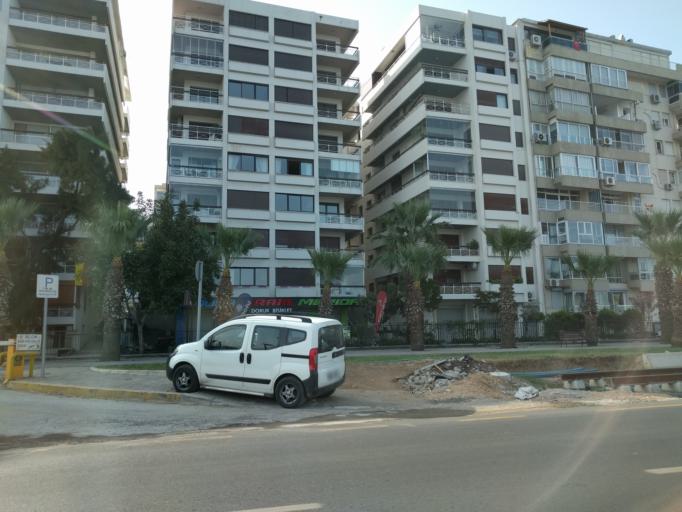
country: TR
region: Izmir
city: Izmir
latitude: 38.4065
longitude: 27.1000
